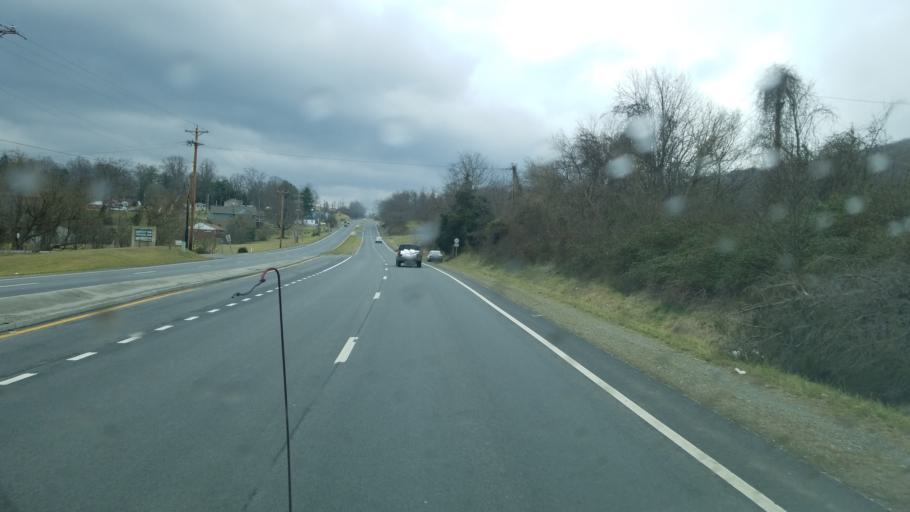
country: US
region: Virginia
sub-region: Giles County
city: Pearisburg
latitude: 37.3174
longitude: -80.7316
